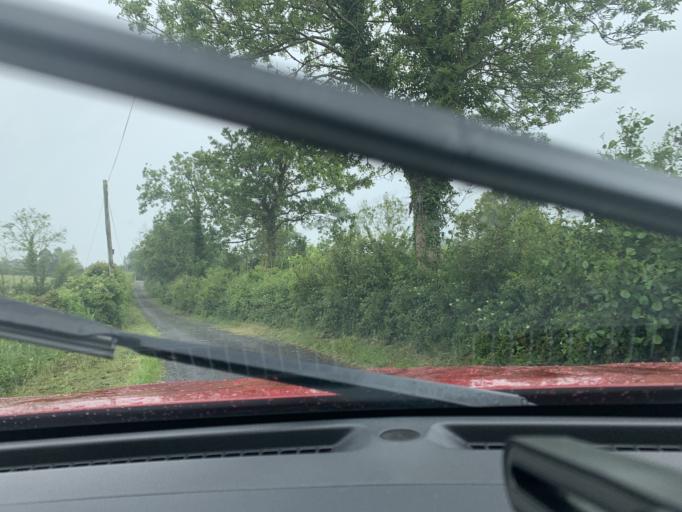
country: GB
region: Northern Ireland
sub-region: Fermanagh District
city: Enniskillen
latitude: 54.2664
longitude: -7.7404
